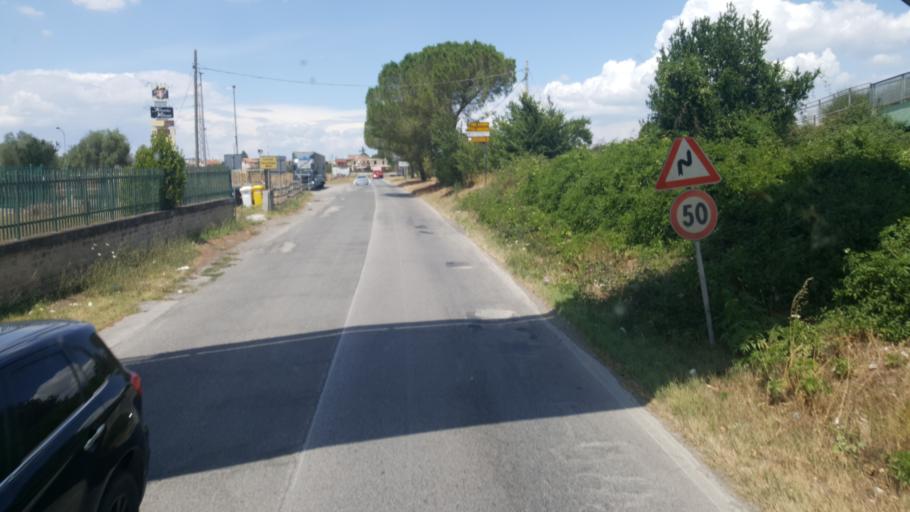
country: IT
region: Latium
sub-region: Citta metropolitana di Roma Capitale
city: Bivio di Capanelle
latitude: 42.1317
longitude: 12.5983
